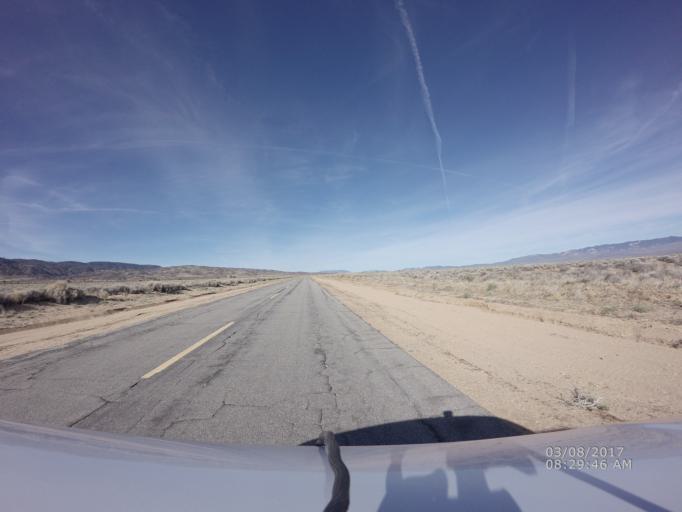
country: US
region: California
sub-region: Los Angeles County
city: Green Valley
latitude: 34.7461
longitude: -118.4773
